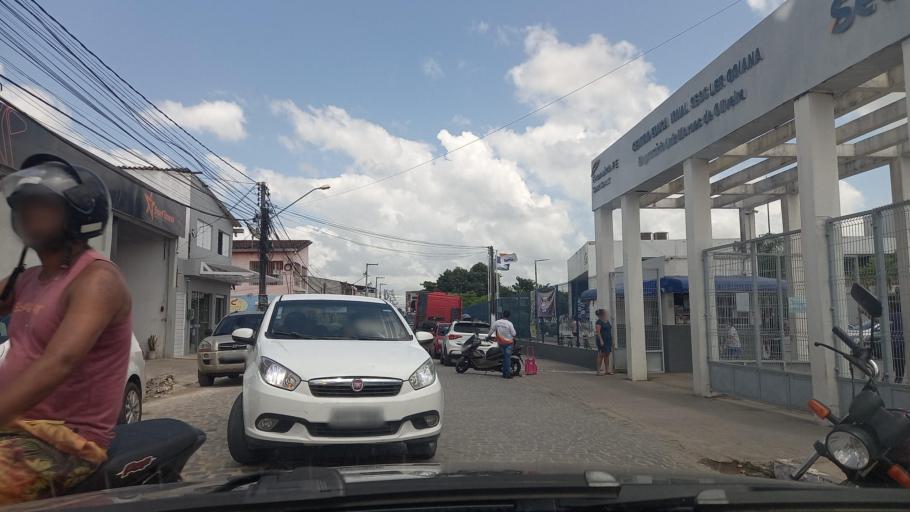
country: BR
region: Pernambuco
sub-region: Goiana
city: Goiana
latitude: -7.5630
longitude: -35.0100
